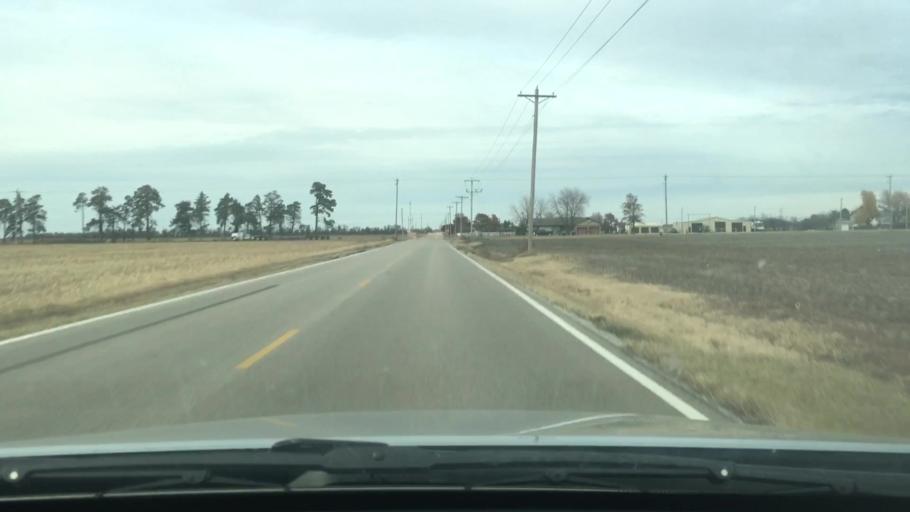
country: US
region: Kansas
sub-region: Sedgwick County
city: Maize
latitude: 37.7780
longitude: -97.4996
